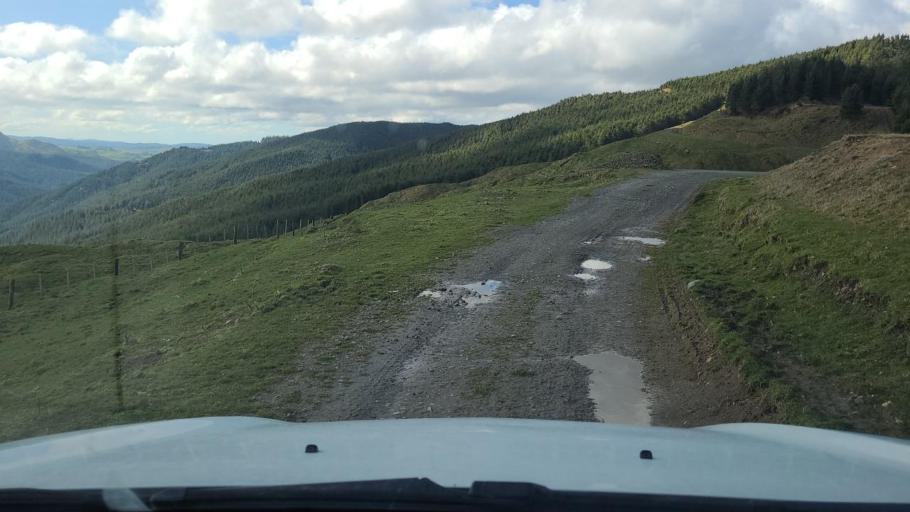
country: NZ
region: Gisborne
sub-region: Gisborne District
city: Gisborne
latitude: -38.1496
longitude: 177.8821
